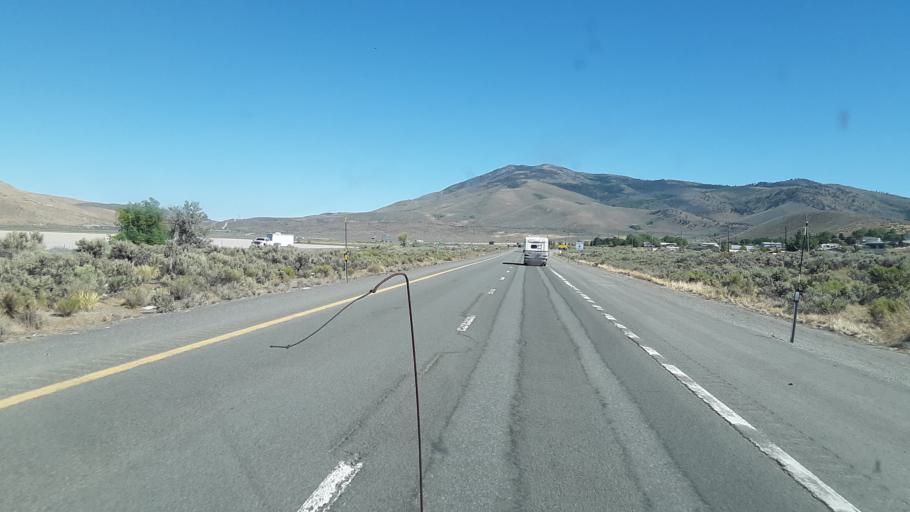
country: US
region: Nevada
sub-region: Washoe County
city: Cold Springs
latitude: 39.6604
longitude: -119.9902
